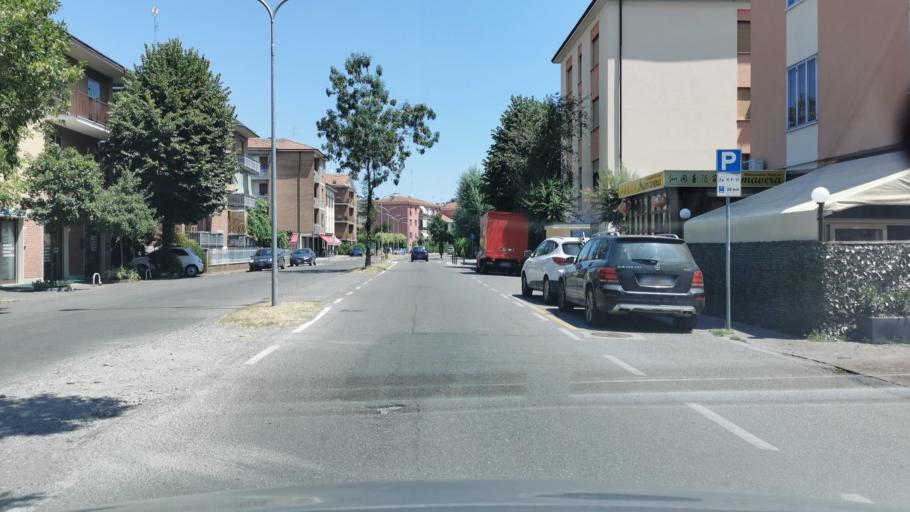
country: IT
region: Emilia-Romagna
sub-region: Provincia di Modena
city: Modena
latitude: 44.6335
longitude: 10.9230
